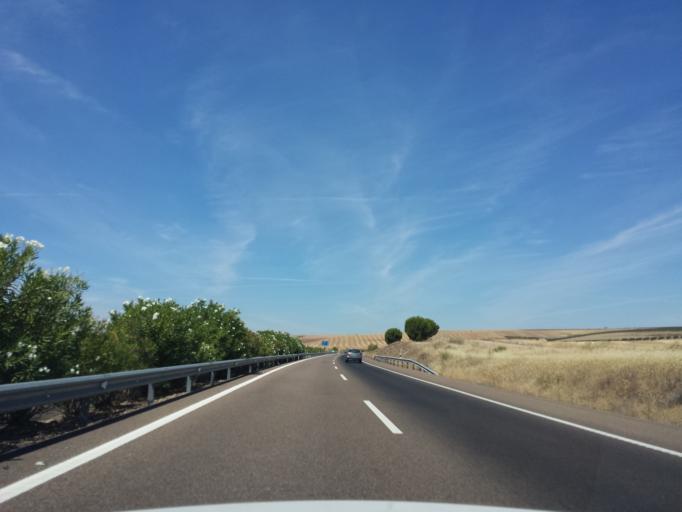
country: ES
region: Extremadura
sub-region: Provincia de Badajoz
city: Merida
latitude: 38.9455
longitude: -6.3118
